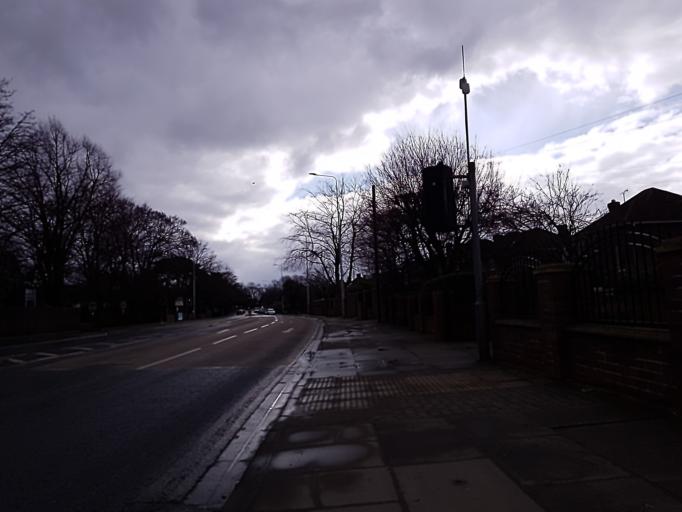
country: GB
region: England
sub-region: North East Lincolnshire
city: Grimbsy
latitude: 53.5575
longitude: -0.0918
